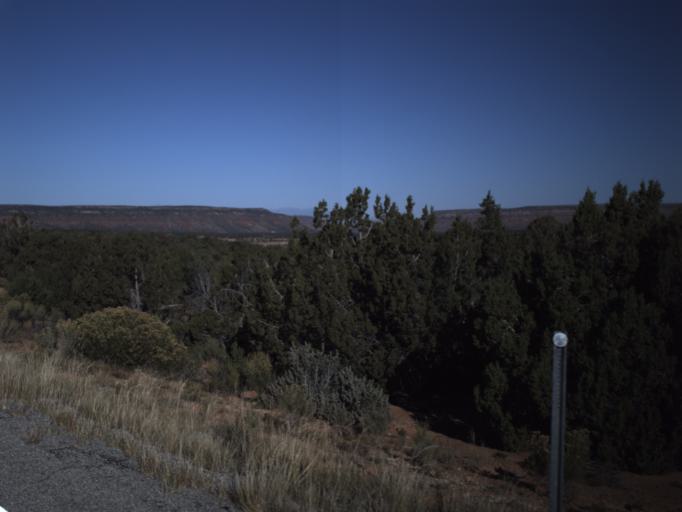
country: US
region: Utah
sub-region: San Juan County
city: Blanding
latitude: 37.5406
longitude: -109.9675
